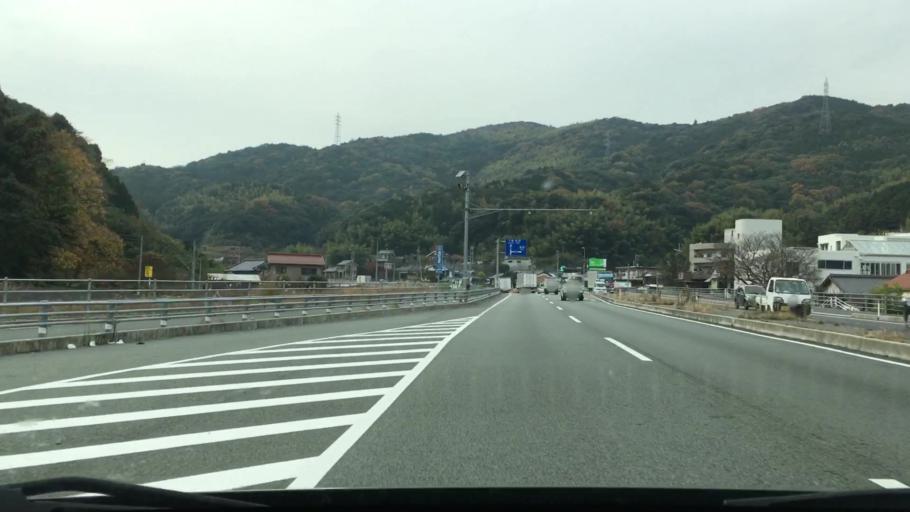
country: JP
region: Yamaguchi
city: Hofu
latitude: 34.0763
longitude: 131.6850
